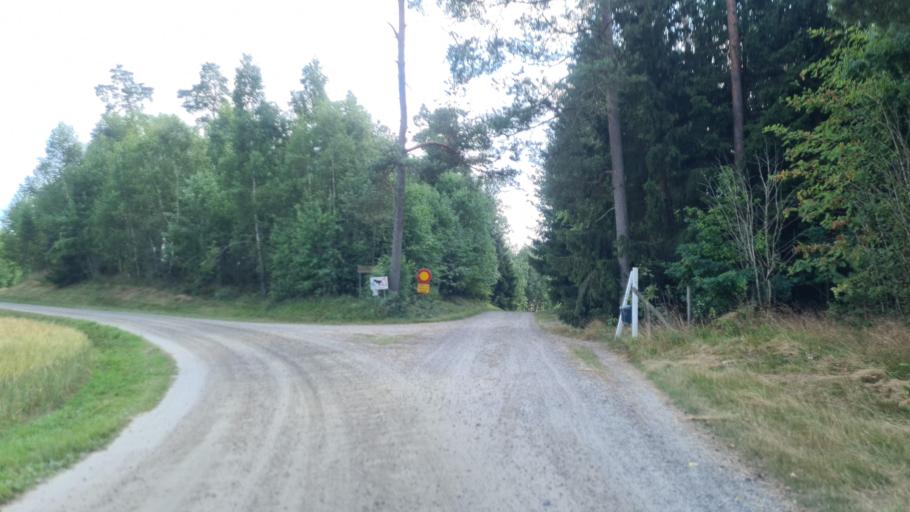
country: SE
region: Kronoberg
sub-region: Ljungby Kommun
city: Ljungby
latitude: 56.7318
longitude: 13.8708
